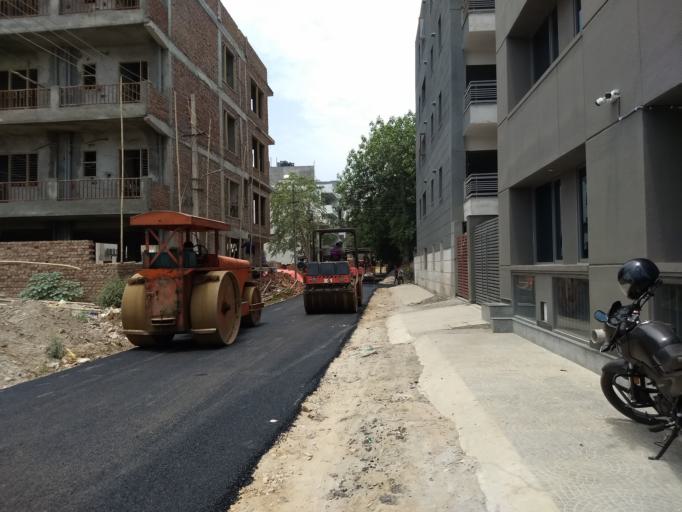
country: IN
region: Haryana
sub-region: Gurgaon
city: Gurgaon
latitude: 28.4487
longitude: 77.0829
